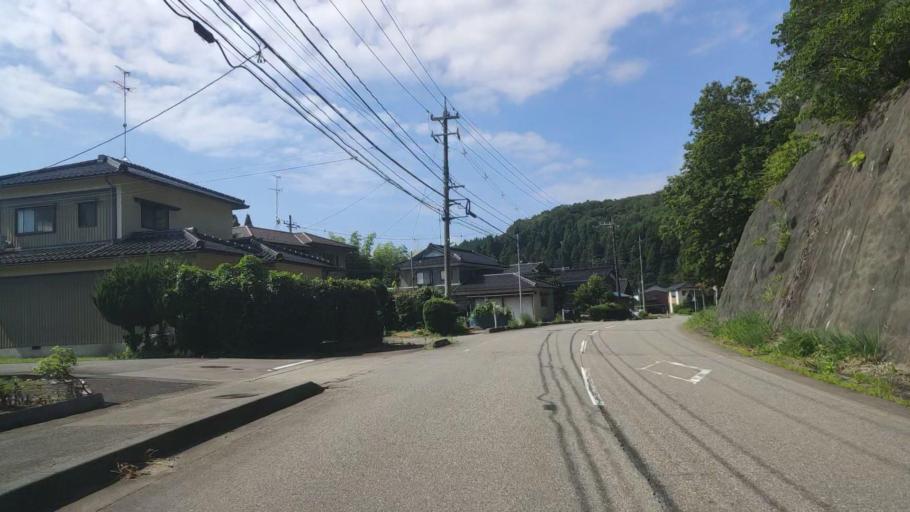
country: JP
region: Ishikawa
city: Komatsu
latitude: 36.3605
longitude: 136.4938
